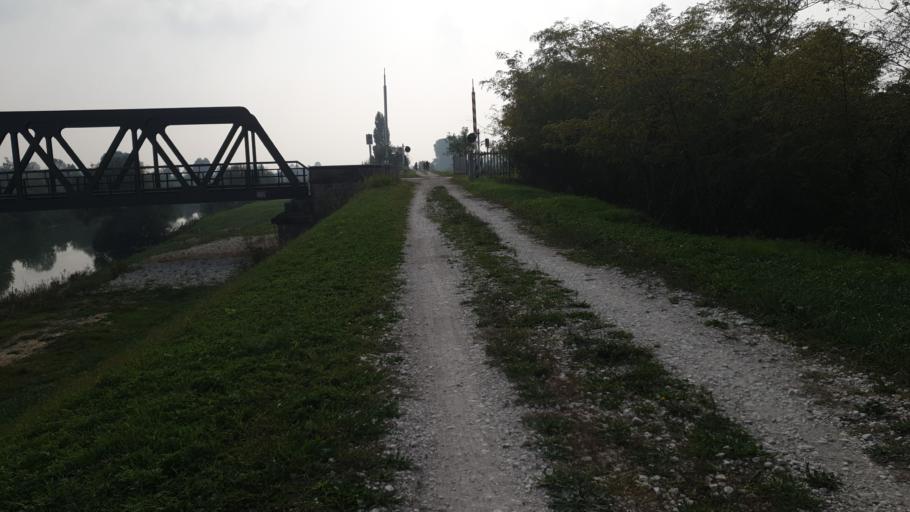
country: IT
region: Veneto
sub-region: Provincia di Padova
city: Corte
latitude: 45.3273
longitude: 12.0652
